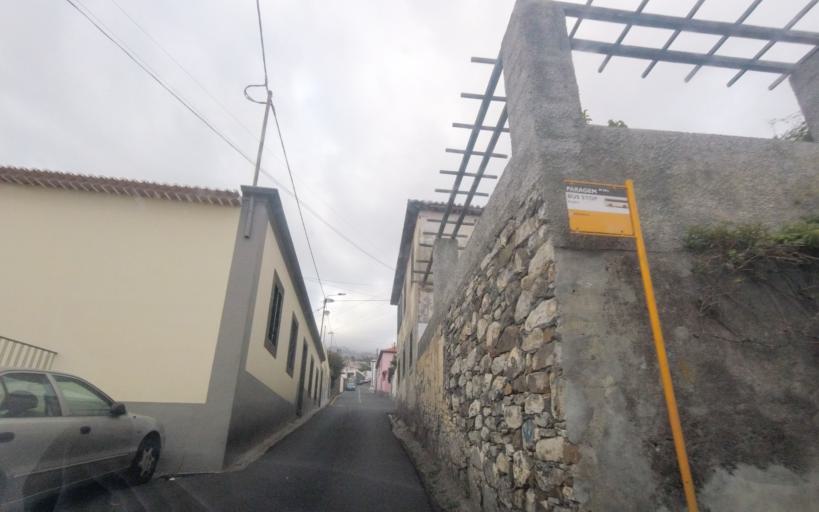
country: PT
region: Madeira
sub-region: Funchal
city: Nossa Senhora do Monte
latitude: 32.6523
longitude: -16.9009
